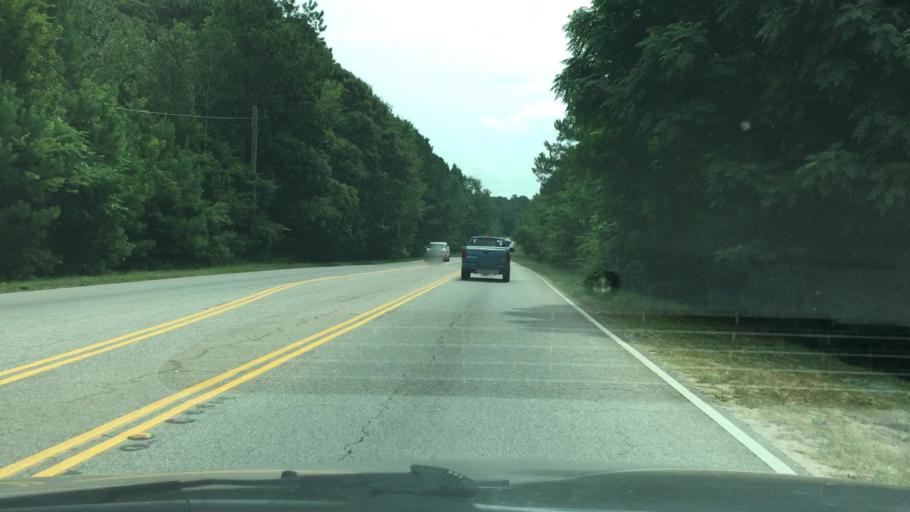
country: US
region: South Carolina
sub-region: Aiken County
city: Warrenville
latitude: 33.5294
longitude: -81.7616
